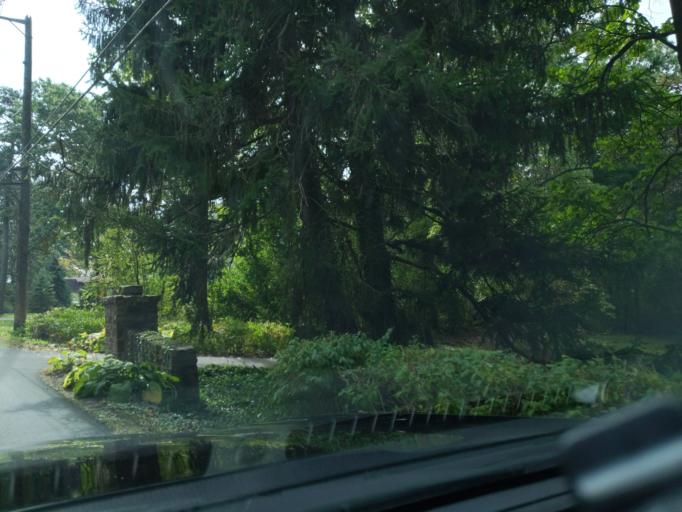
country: US
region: Pennsylvania
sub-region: Blair County
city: Lakemont
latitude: 40.4509
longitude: -78.3882
